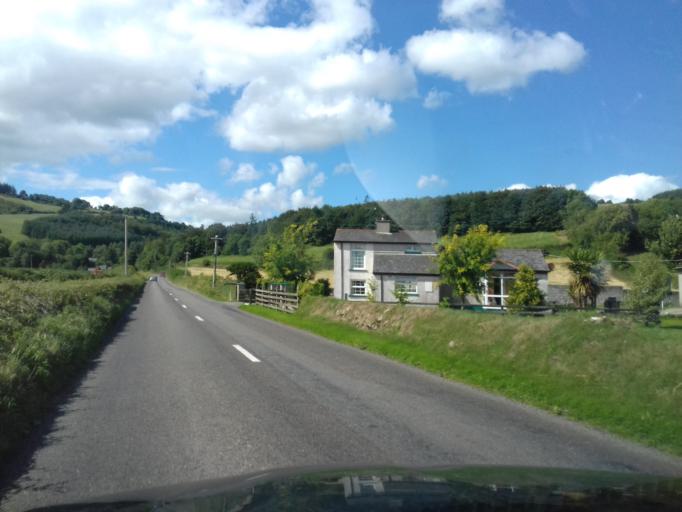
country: IE
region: Munster
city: Carrick-on-Suir
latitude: 52.3996
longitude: -7.4774
